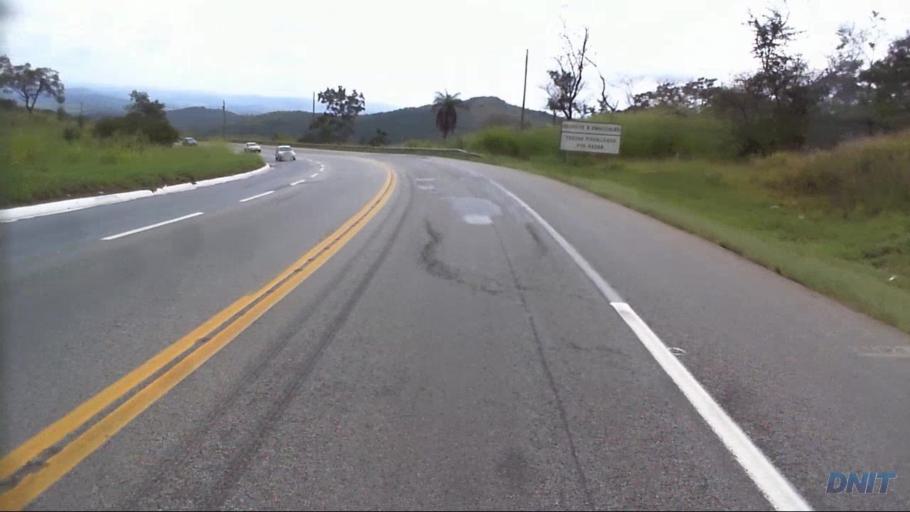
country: BR
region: Minas Gerais
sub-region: Caete
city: Caete
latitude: -19.7867
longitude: -43.7106
